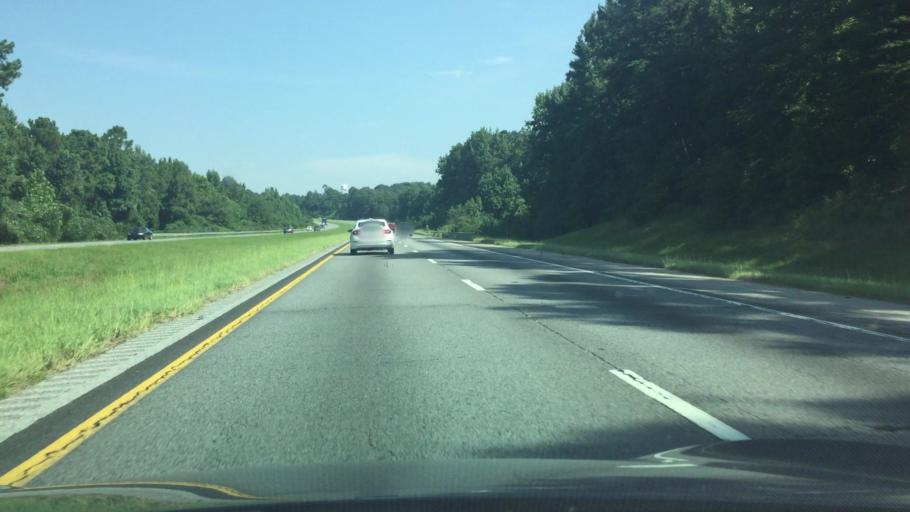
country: US
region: Alabama
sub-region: Autauga County
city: Pine Level
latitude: 32.6034
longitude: -86.4785
